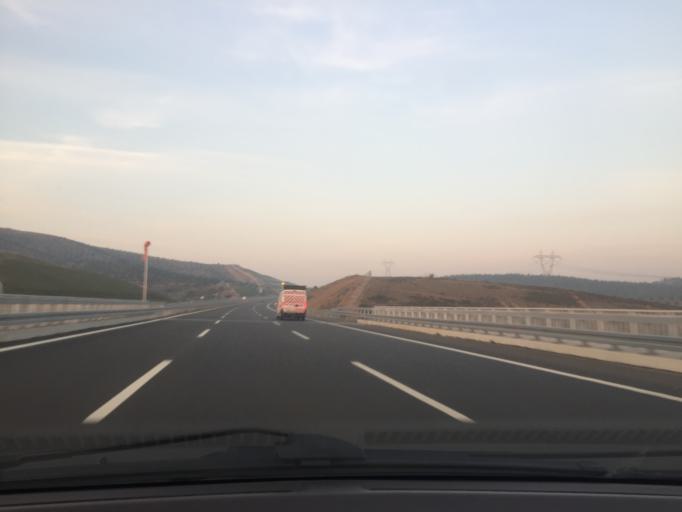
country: TR
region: Bursa
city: Mahmudiye
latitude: 40.2745
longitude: 28.5661
